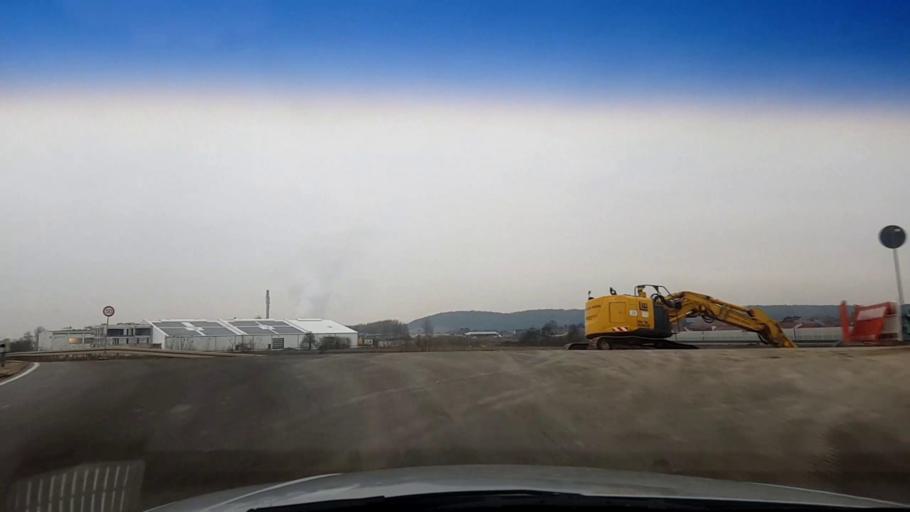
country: DE
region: Bavaria
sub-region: Upper Franconia
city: Zapfendorf
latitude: 50.0148
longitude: 10.9239
